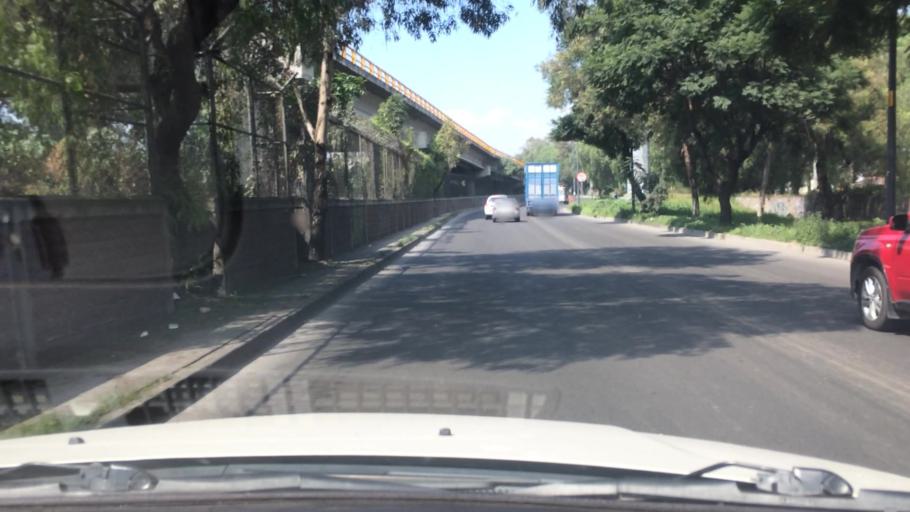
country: MX
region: Mexico
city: Colonia Lindavista
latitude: 19.5190
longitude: -99.1438
